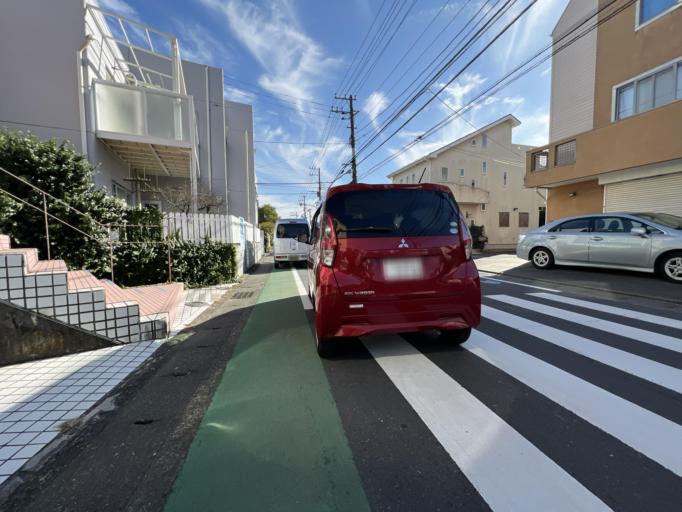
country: JP
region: Kanagawa
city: Kamakura
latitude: 35.3099
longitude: 139.5484
